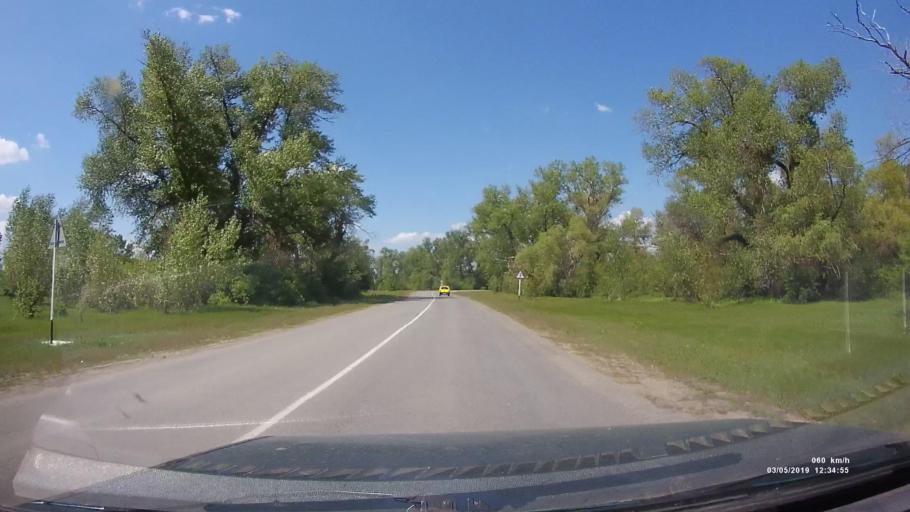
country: RU
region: Rostov
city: Semikarakorsk
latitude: 47.5236
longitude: 40.7639
